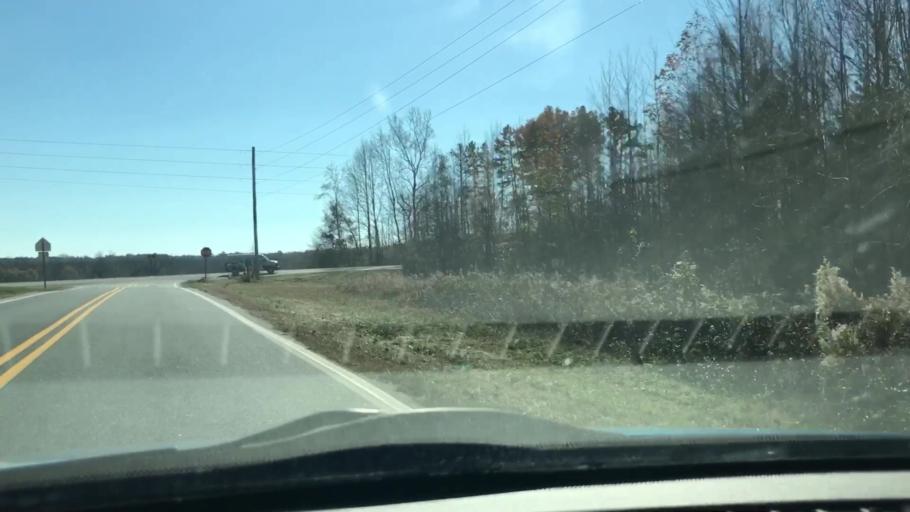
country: US
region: North Carolina
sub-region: Davidson County
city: Denton
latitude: 35.6403
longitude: -79.9721
